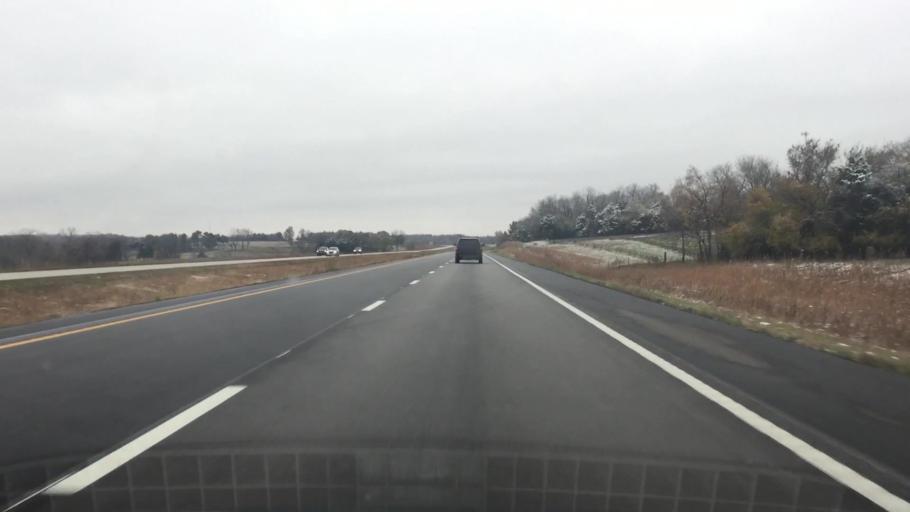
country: US
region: Missouri
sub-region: Saint Clair County
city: Osceola
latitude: 37.9985
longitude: -93.6543
